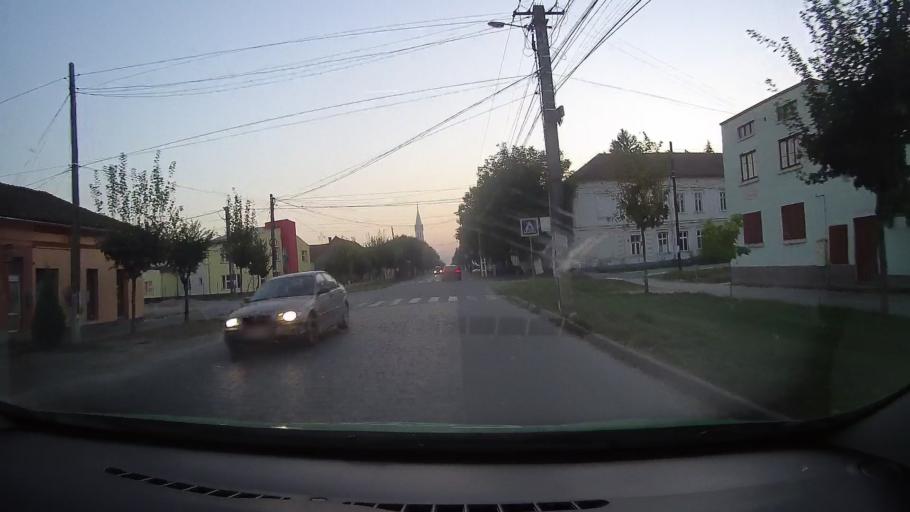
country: RO
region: Arad
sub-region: Comuna Santana
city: Santana
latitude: 46.3440
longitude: 21.4999
